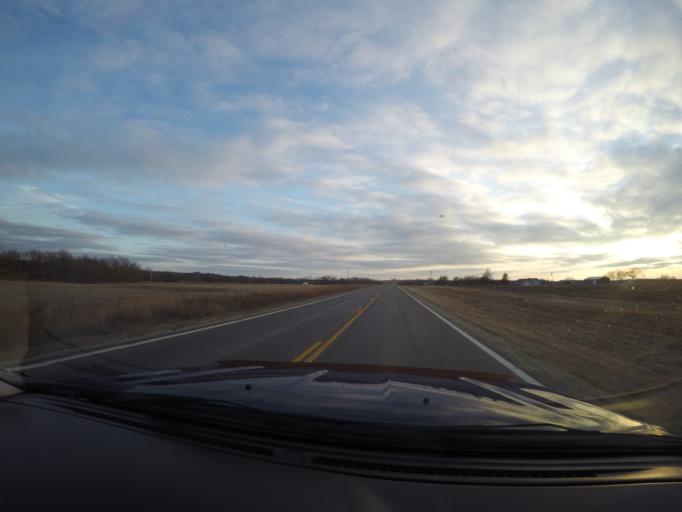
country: US
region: Kansas
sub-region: Morris County
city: Council Grove
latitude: 38.6064
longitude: -96.4989
